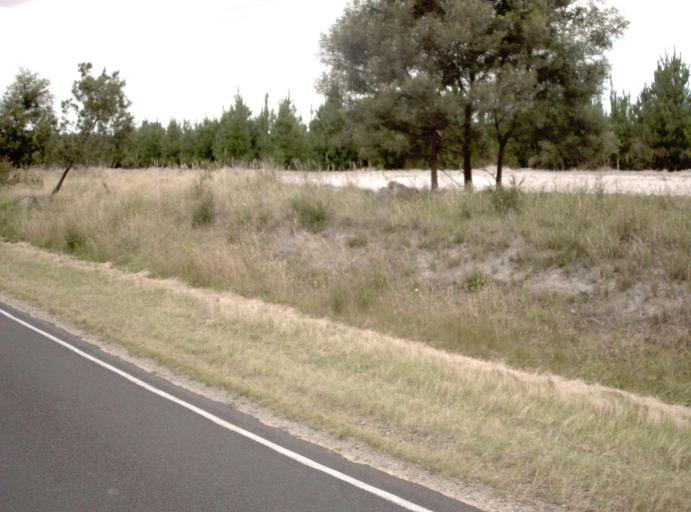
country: AU
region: Victoria
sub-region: Wellington
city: Sale
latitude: -38.1718
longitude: 147.0223
